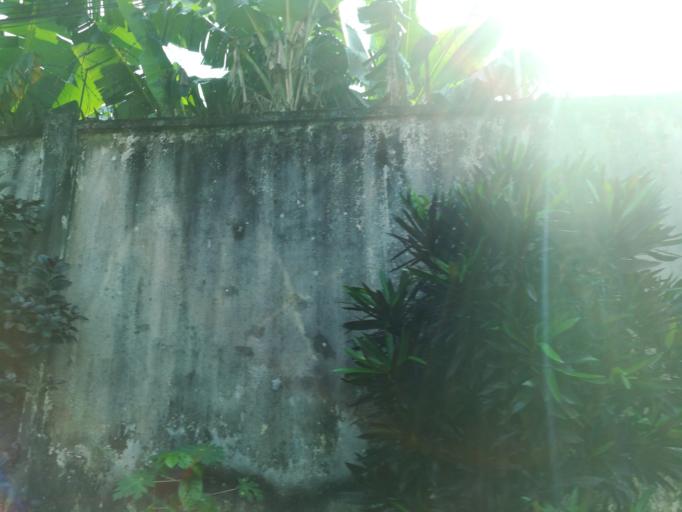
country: NG
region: Rivers
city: Port Harcourt
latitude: 4.8321
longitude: 6.9855
